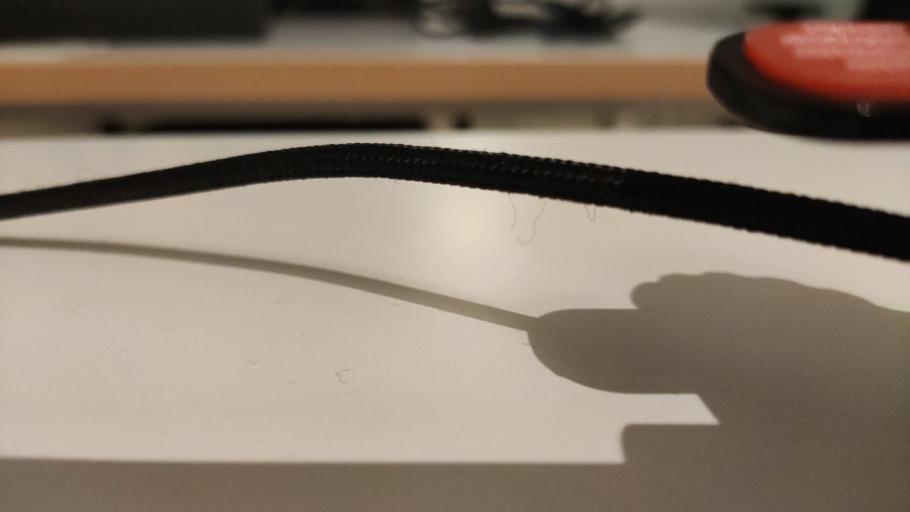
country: RU
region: Moskovskaya
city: Gorshkovo
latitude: 56.3692
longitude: 37.4418
